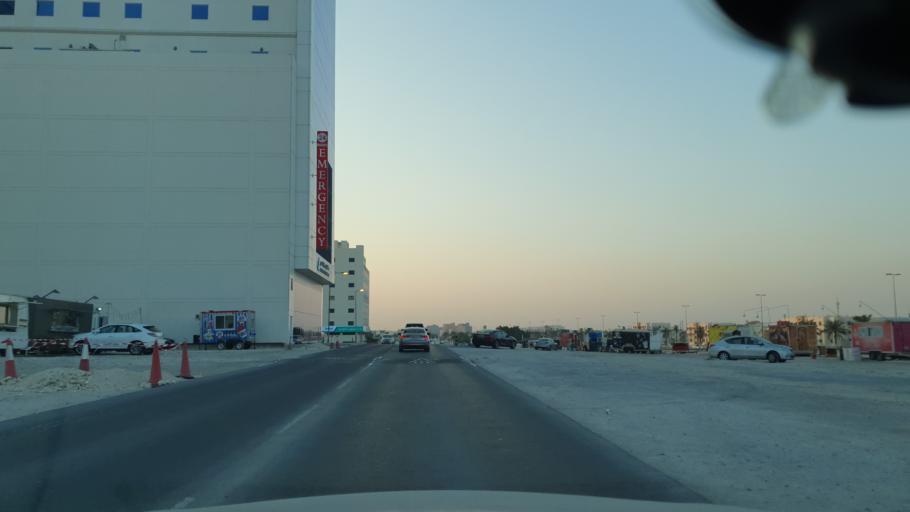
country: BH
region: Northern
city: Ar Rifa'
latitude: 26.1540
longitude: 50.5694
